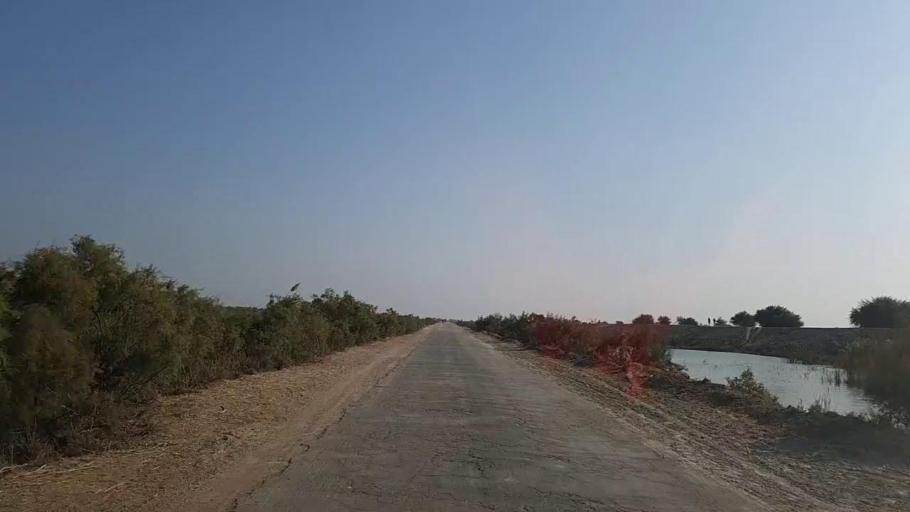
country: PK
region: Sindh
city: Sanghar
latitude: 25.9679
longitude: 69.0337
